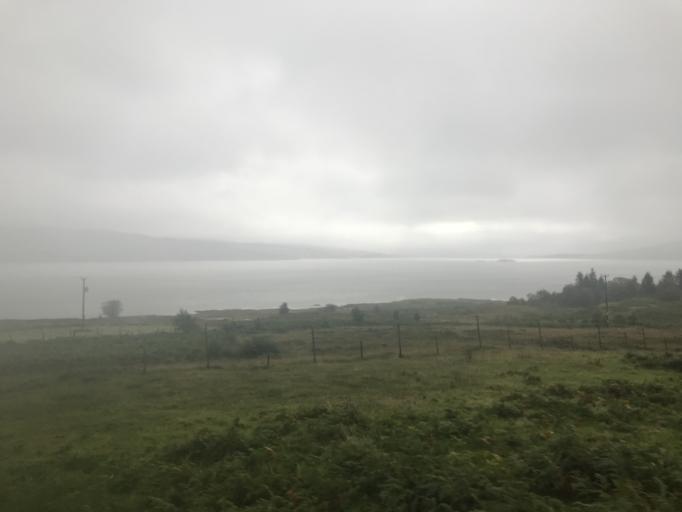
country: GB
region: Scotland
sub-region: Argyll and Bute
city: Isle Of Mull
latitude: 56.5453
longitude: -5.9757
